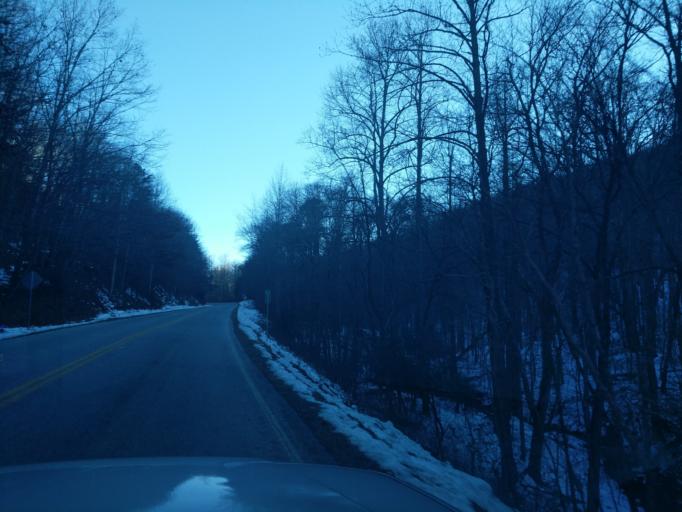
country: US
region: Georgia
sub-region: Towns County
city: Hiawassee
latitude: 34.9151
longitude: -83.6226
